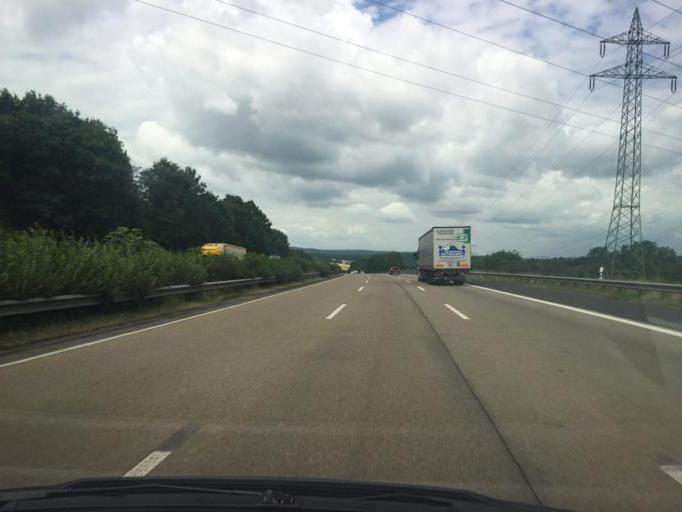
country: DE
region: Rheinland-Pfalz
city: Grossholbach
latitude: 50.4540
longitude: 7.8924
